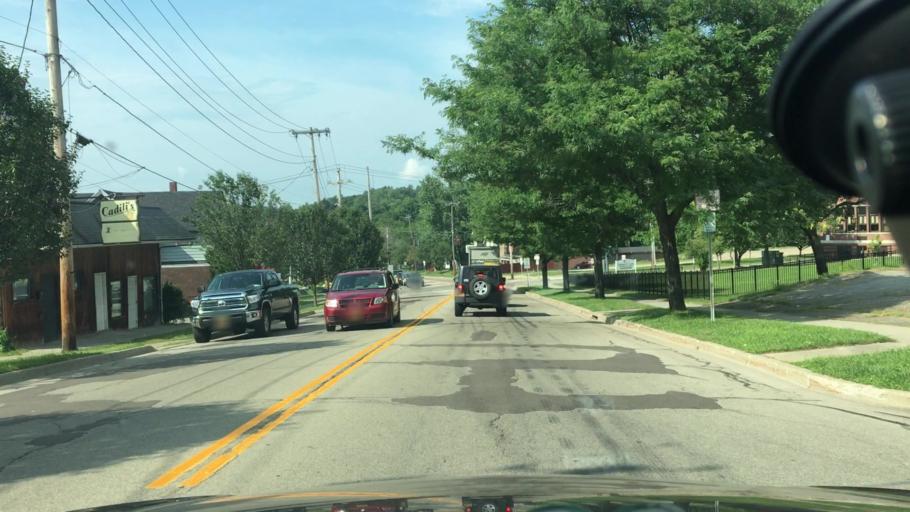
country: US
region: New York
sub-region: Chautauqua County
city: Jamestown
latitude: 42.1000
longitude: -79.2418
